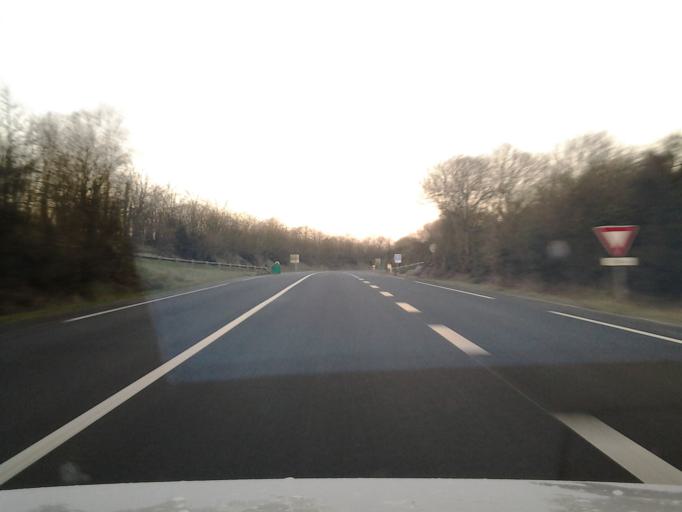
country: FR
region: Pays de la Loire
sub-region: Departement de la Vendee
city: Les Epesses
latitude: 46.8992
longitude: -0.9308
